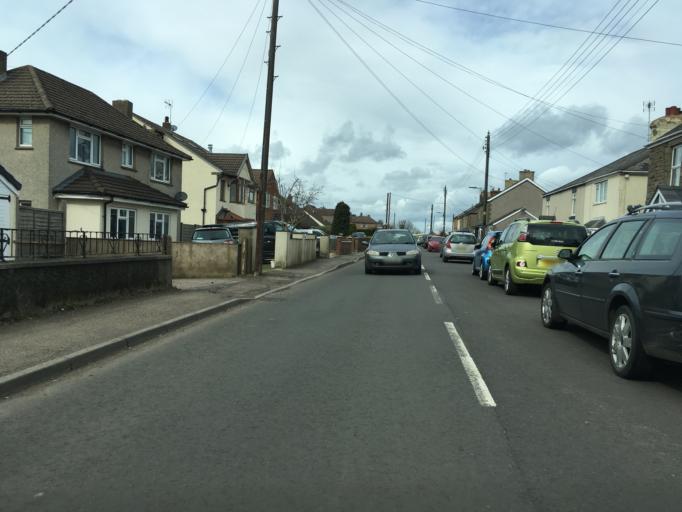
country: GB
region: England
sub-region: Gloucestershire
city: Coleford
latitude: 51.7805
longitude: -2.6075
